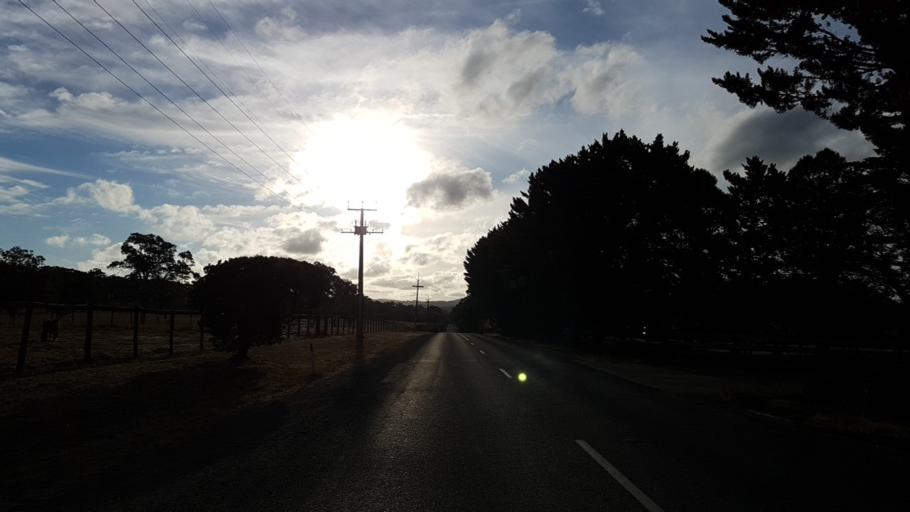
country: AU
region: South Australia
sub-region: Adelaide Hills
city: Woodside
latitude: -34.9767
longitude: 138.8696
